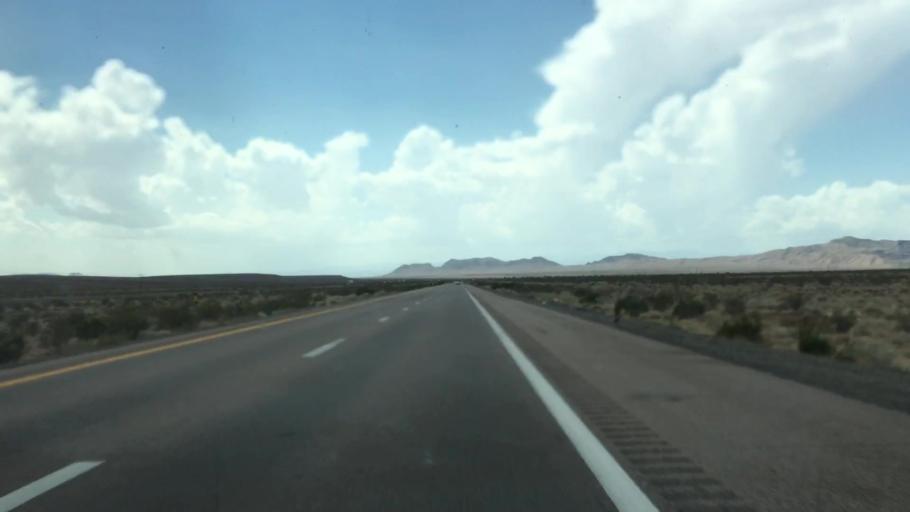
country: US
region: Nevada
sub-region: Clark County
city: Moapa Valley
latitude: 36.7606
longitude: -114.3668
